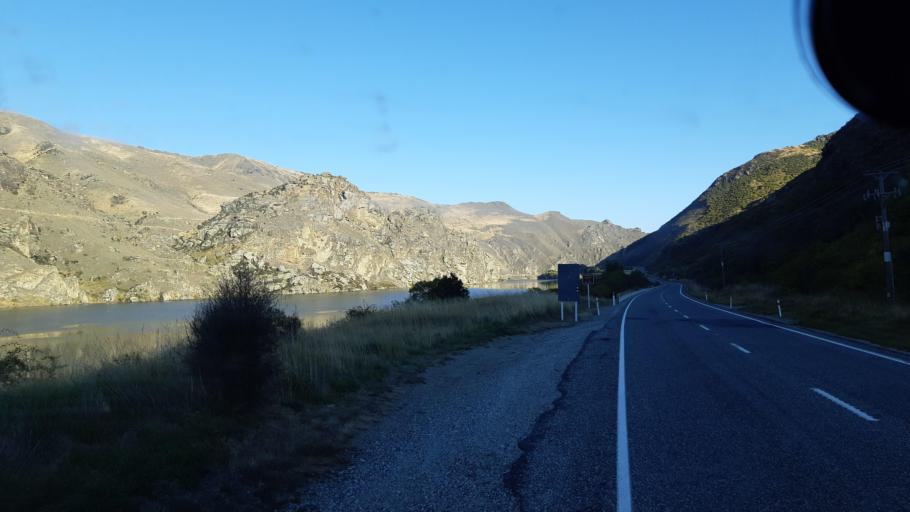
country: NZ
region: Otago
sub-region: Queenstown-Lakes District
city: Wanaka
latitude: -45.0832
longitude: 169.2584
